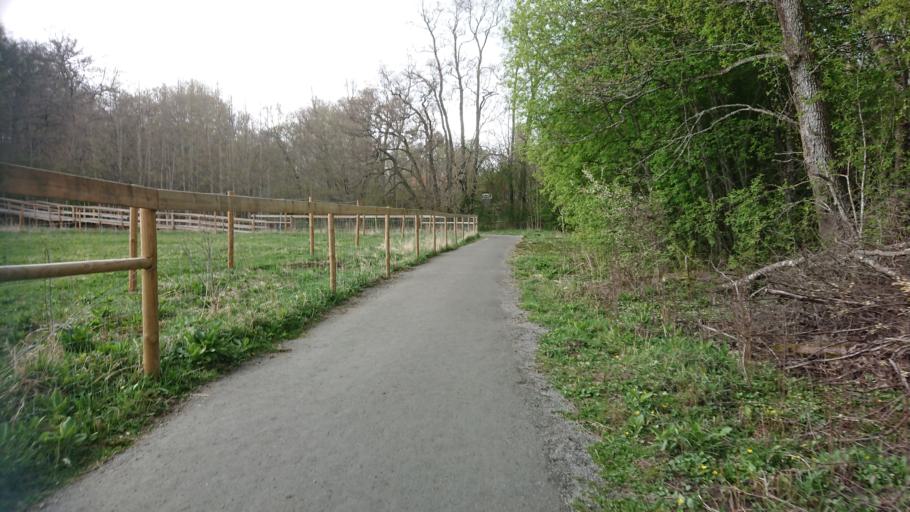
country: SE
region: Uppsala
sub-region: Uppsala Kommun
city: Uppsala
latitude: 59.7996
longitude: 17.6068
